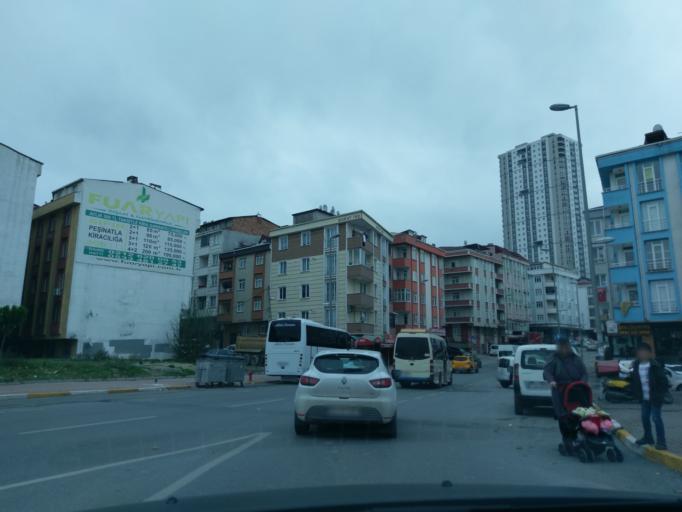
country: TR
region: Istanbul
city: Esenyurt
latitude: 41.0204
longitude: 28.6702
